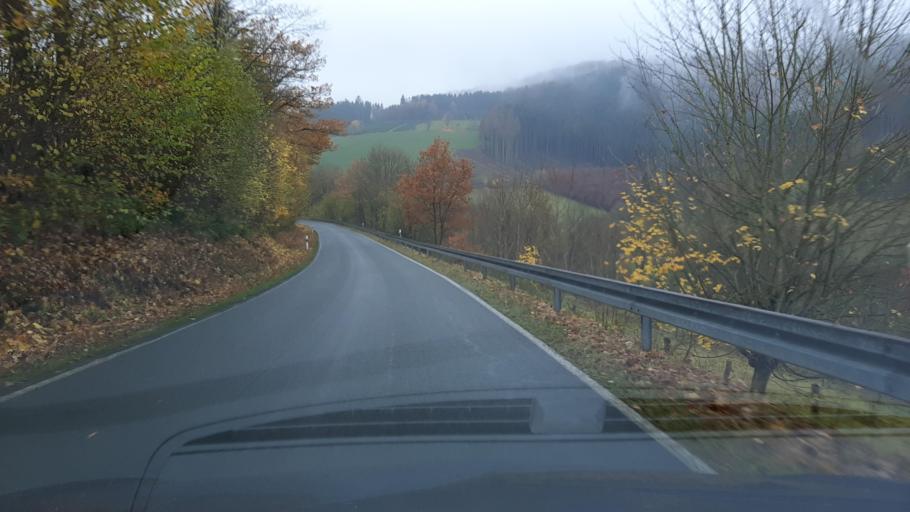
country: DE
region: North Rhine-Westphalia
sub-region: Regierungsbezirk Arnsberg
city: Olsberg
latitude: 51.2872
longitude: 8.4847
